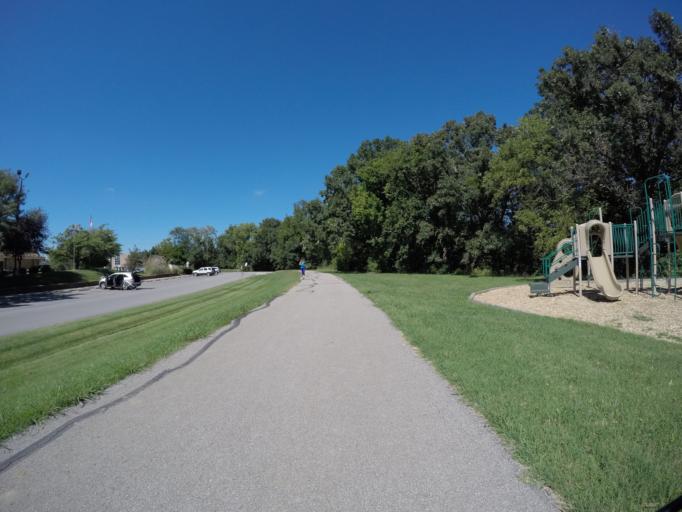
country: US
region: Kansas
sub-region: Johnson County
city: Overland Park
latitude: 38.9405
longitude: -94.6618
